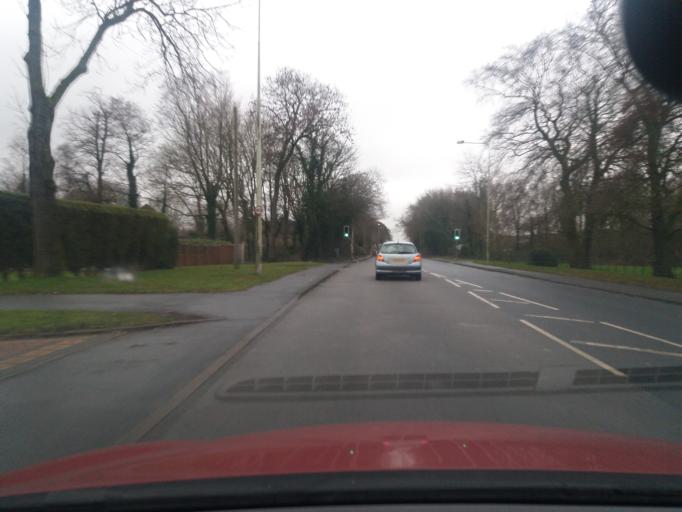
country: GB
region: England
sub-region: Lancashire
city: Clayton-le-Woods
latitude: 53.7104
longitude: -2.6420
